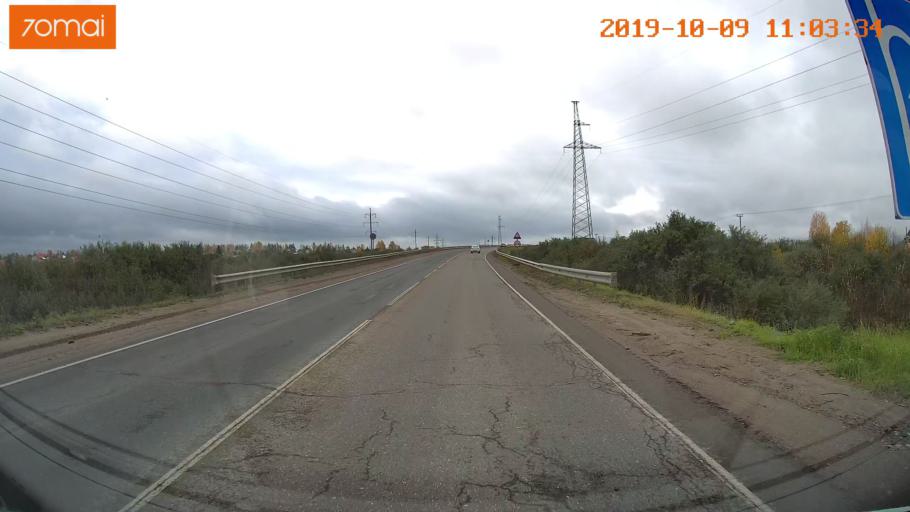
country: RU
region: Vologda
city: Vologda
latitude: 59.2206
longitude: 39.7741
